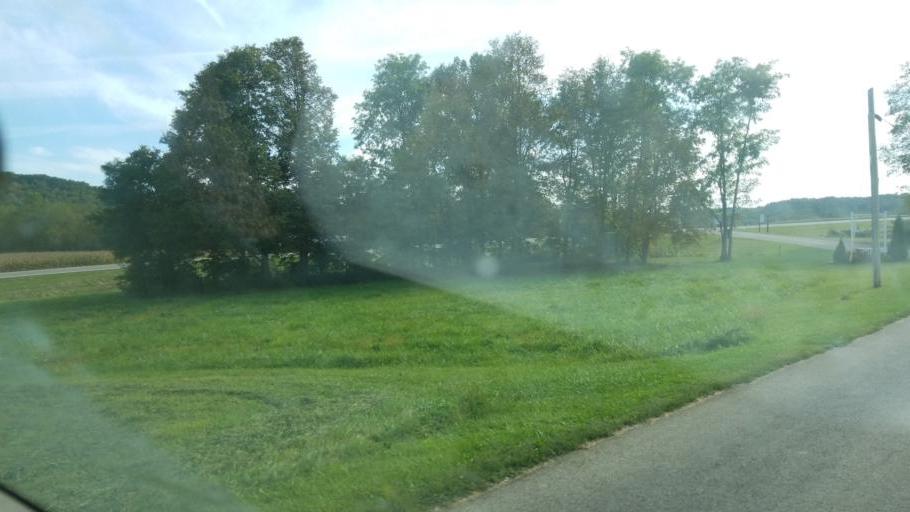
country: US
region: Ohio
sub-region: Knox County
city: Danville
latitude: 40.4578
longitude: -82.2222
